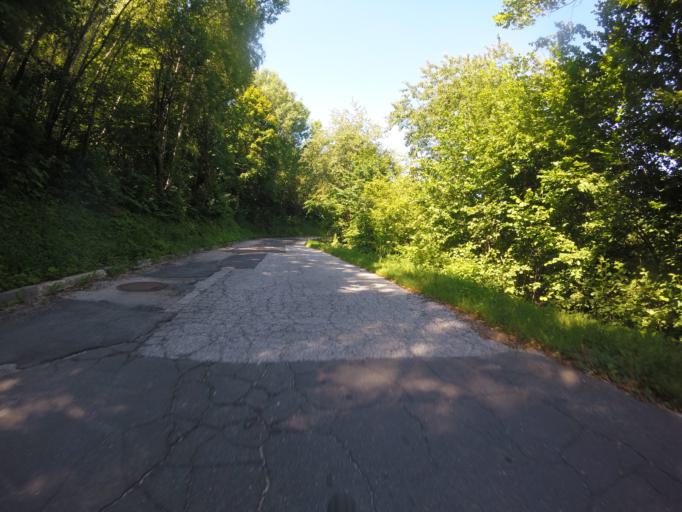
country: SI
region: Brezice
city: Brezice
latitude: 45.8184
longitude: 15.5364
